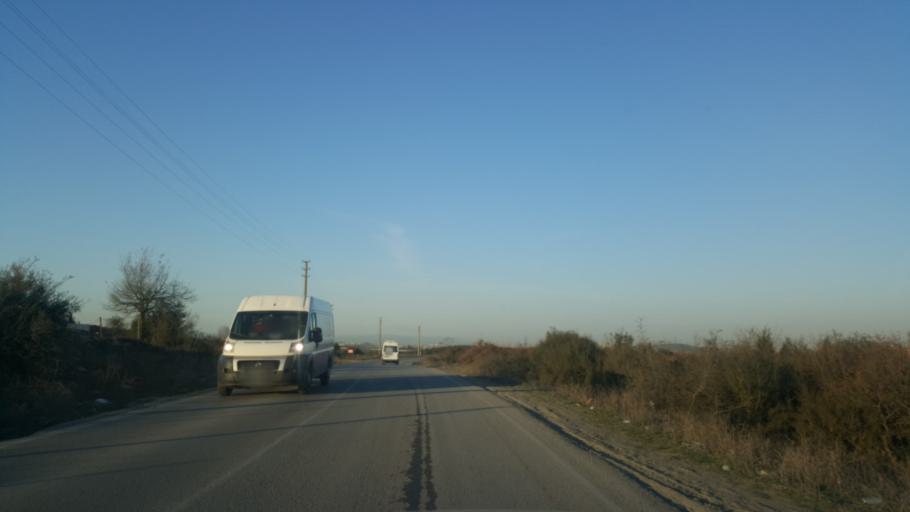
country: TR
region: Kocaeli
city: Tavsanli
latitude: 40.8451
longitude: 29.5477
